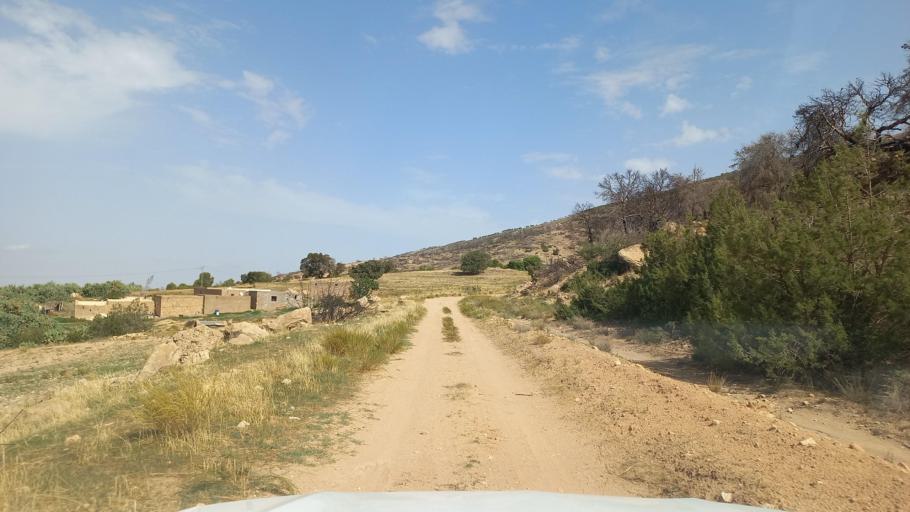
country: TN
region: Al Qasrayn
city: Kasserine
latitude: 35.3534
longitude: 8.8933
